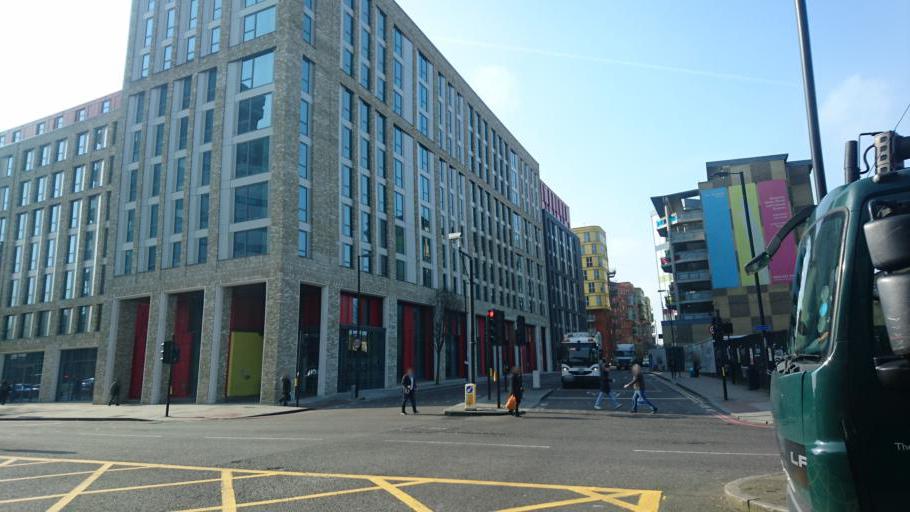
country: GB
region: England
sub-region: Greater London
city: Holloway
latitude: 51.5527
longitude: -0.1125
